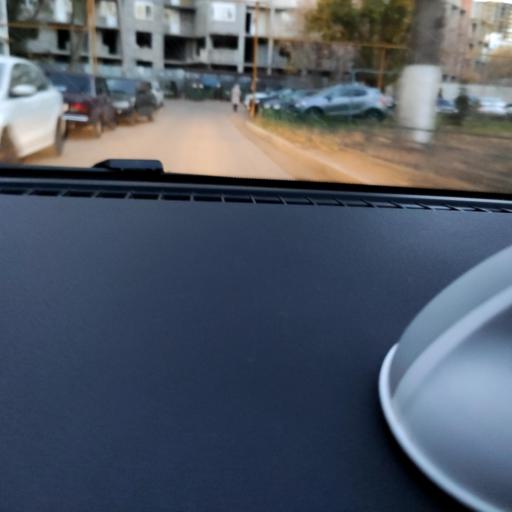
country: RU
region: Samara
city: Samara
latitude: 53.2511
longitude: 50.2314
